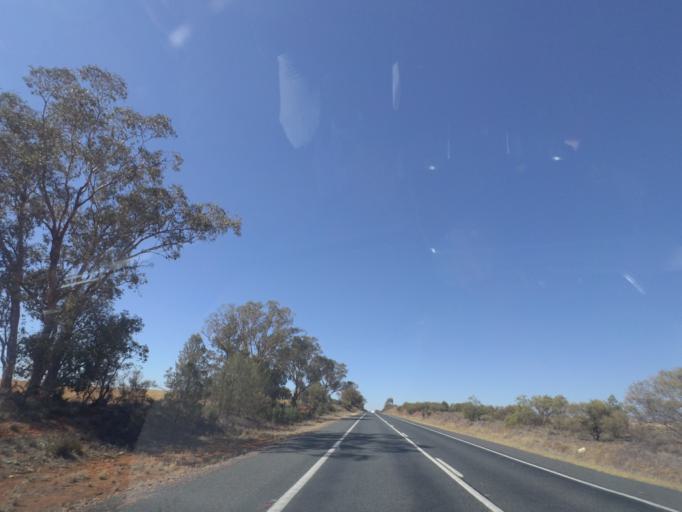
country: AU
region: New South Wales
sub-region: Bland
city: West Wyalong
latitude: -34.1777
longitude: 147.1139
